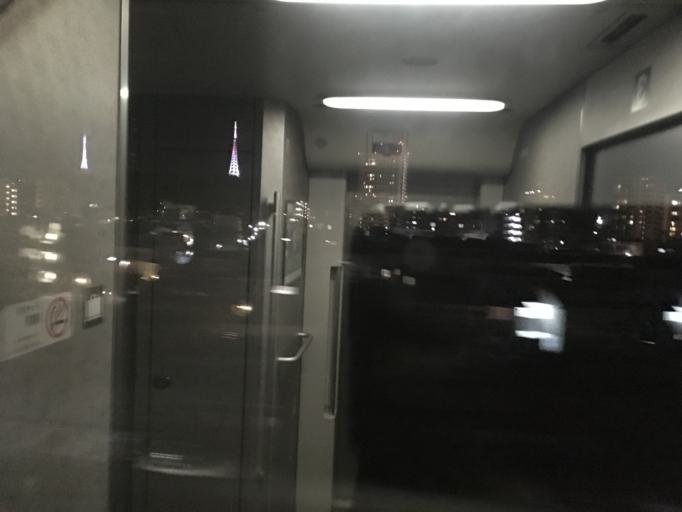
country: JP
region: Miyagi
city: Sendai
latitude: 38.2374
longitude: 140.8934
